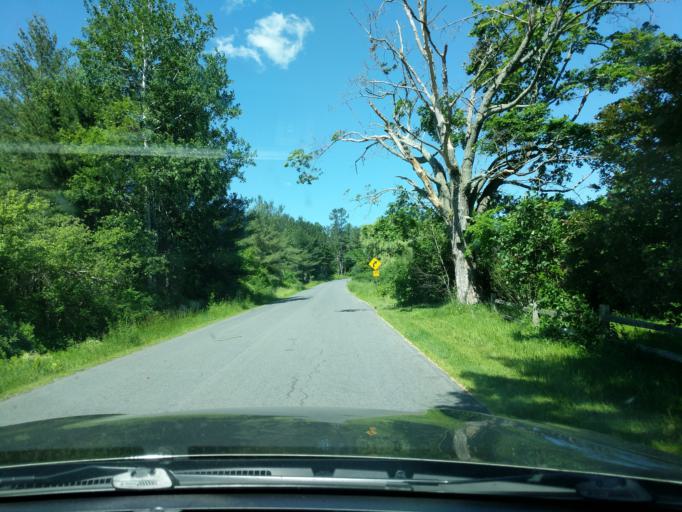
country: US
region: New York
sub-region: Tompkins County
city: Dryden
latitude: 42.3792
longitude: -76.3581
